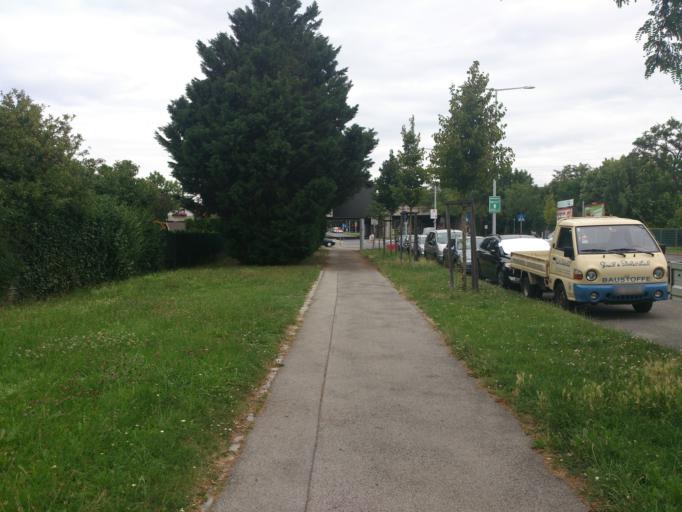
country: AT
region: Lower Austria
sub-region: Politischer Bezirk Modling
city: Vosendorf
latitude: 48.1584
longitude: 16.3344
